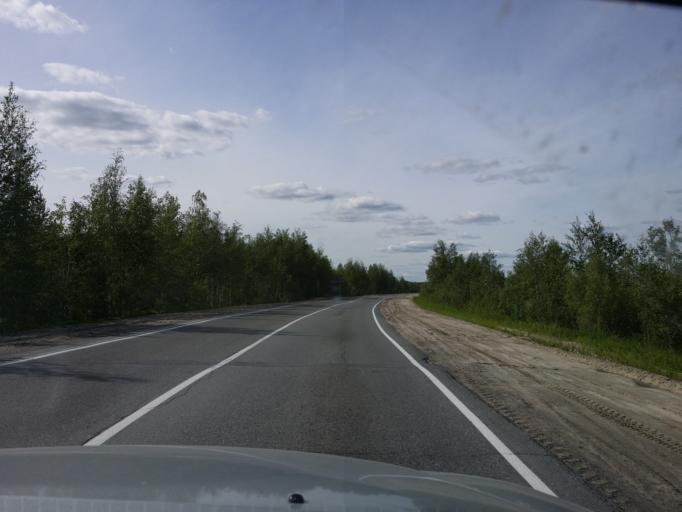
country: RU
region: Khanty-Mansiyskiy Avtonomnyy Okrug
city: Nizhnevartovsk
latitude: 61.1059
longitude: 76.6134
